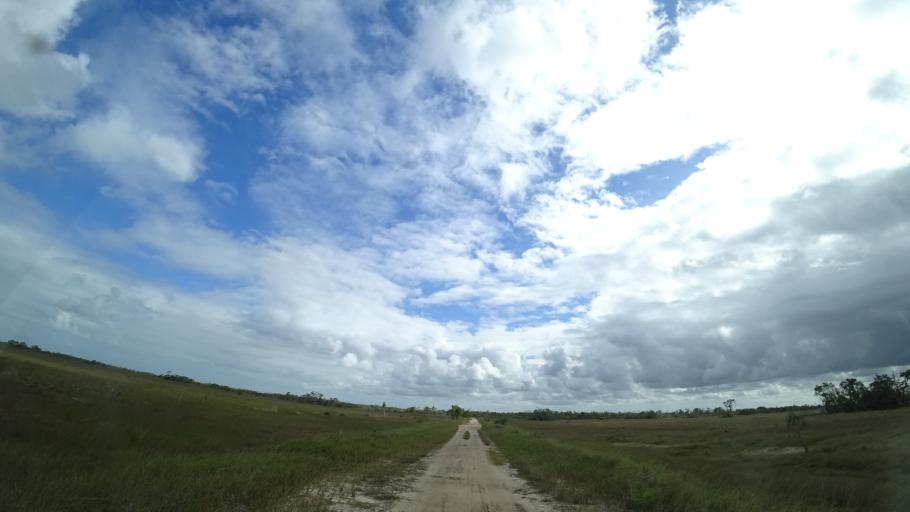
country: MZ
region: Sofala
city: Beira
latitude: -19.5784
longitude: 35.1860
